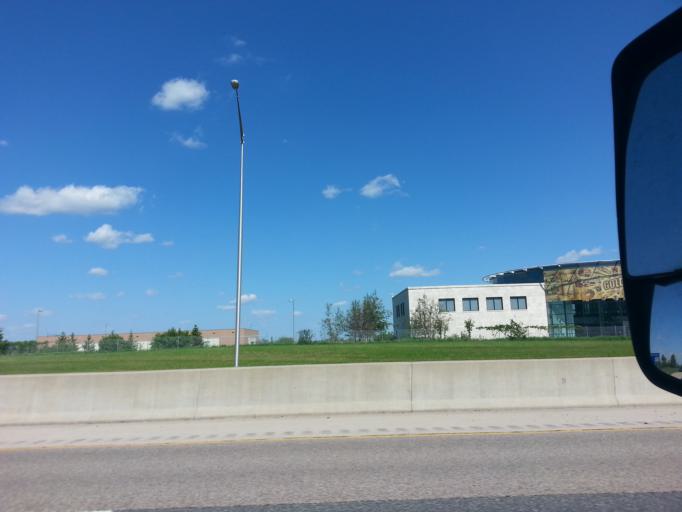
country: US
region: Illinois
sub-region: Winnebago County
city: Cherry Valley
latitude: 42.2636
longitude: -88.9650
